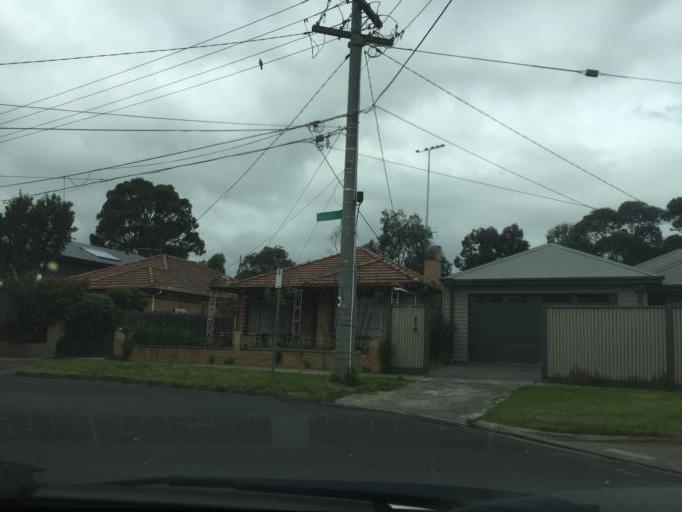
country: AU
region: Victoria
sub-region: Hobsons Bay
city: South Kingsville
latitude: -37.8197
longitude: 144.8705
